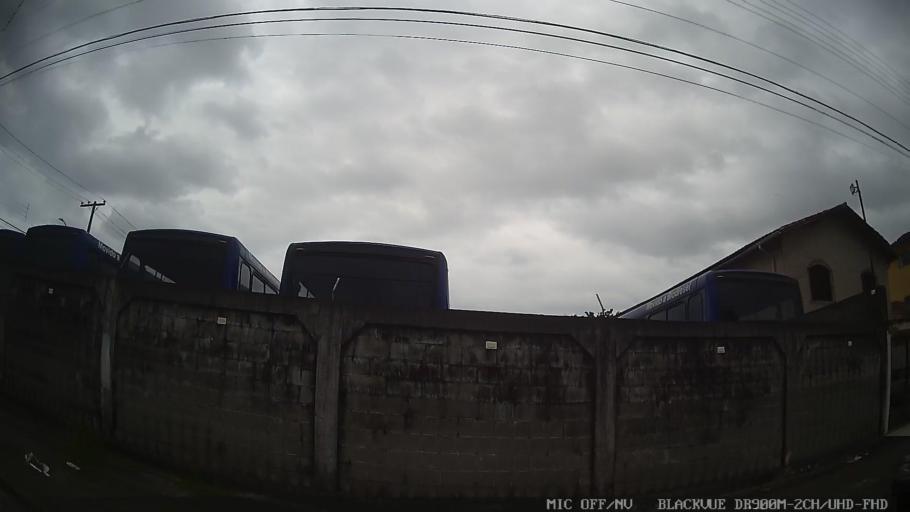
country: BR
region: Sao Paulo
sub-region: Guaruja
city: Guaruja
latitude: -23.9930
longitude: -46.2729
